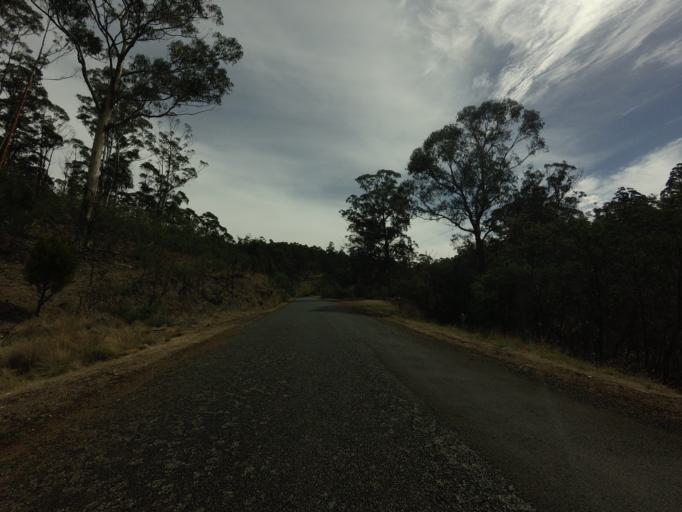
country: AU
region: Tasmania
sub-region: Sorell
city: Sorell
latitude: -42.5661
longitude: 147.6820
